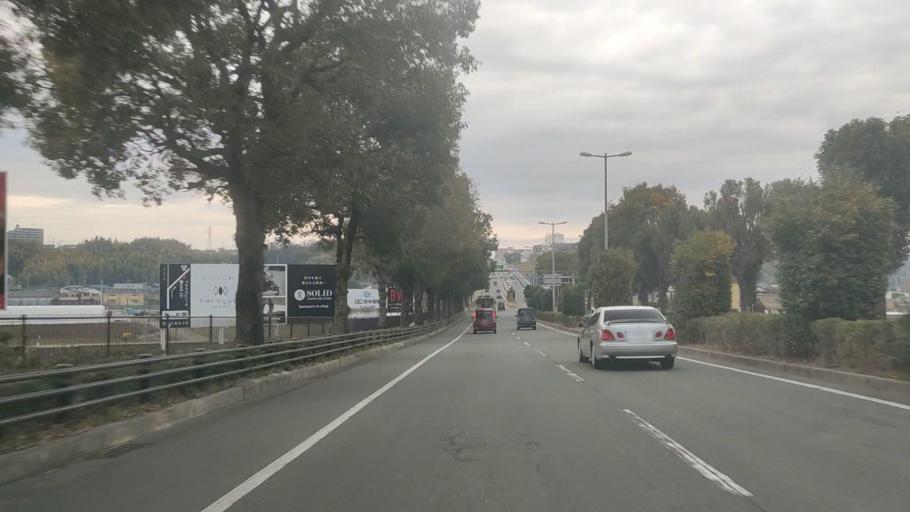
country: JP
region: Kumamoto
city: Ozu
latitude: 32.8445
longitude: 130.7811
